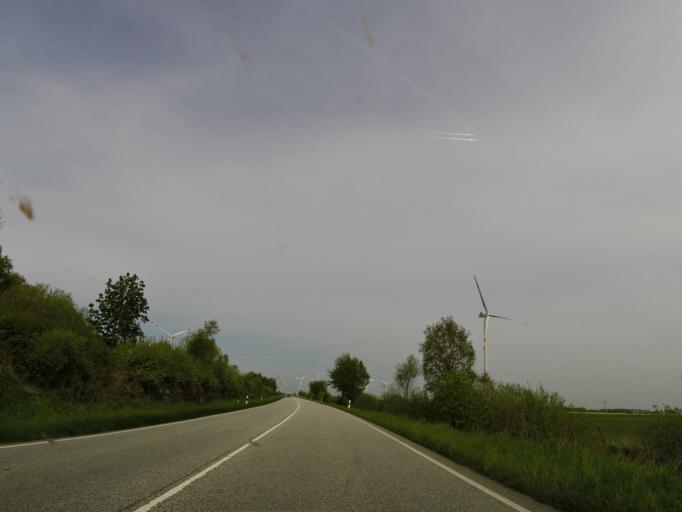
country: DE
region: Schleswig-Holstein
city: Stelle-Wittenwurth
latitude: 54.2473
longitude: 9.0395
